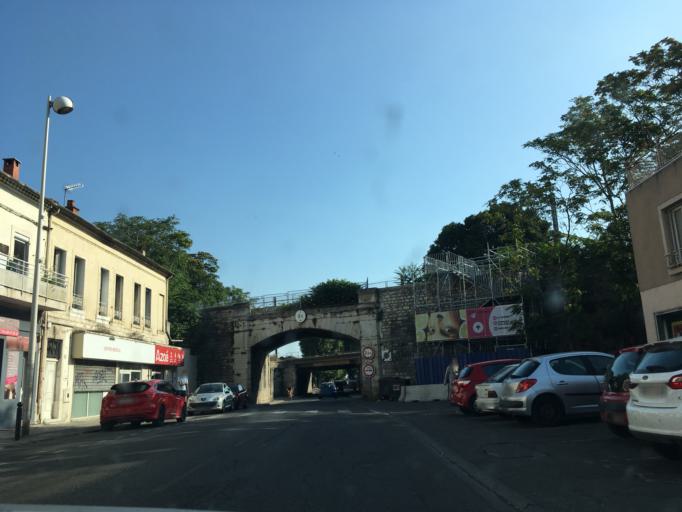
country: FR
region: Provence-Alpes-Cote d'Azur
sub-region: Departement des Bouches-du-Rhone
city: Arles
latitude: 43.6825
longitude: 4.6322
